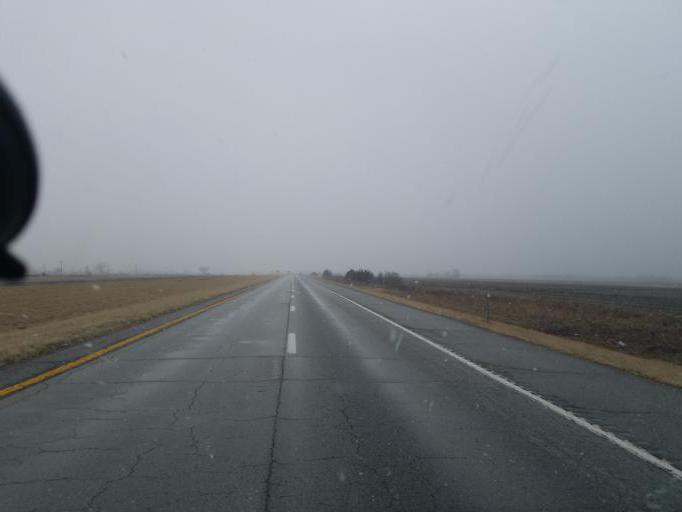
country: US
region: Missouri
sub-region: Macon County
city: La Plata
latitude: 39.9443
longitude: -92.4772
